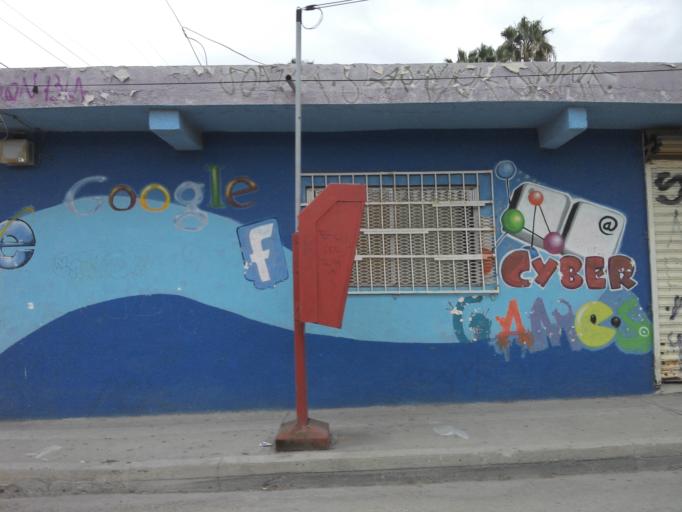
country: US
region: California
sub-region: San Diego County
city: Imperial Beach
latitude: 32.5264
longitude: -117.0815
